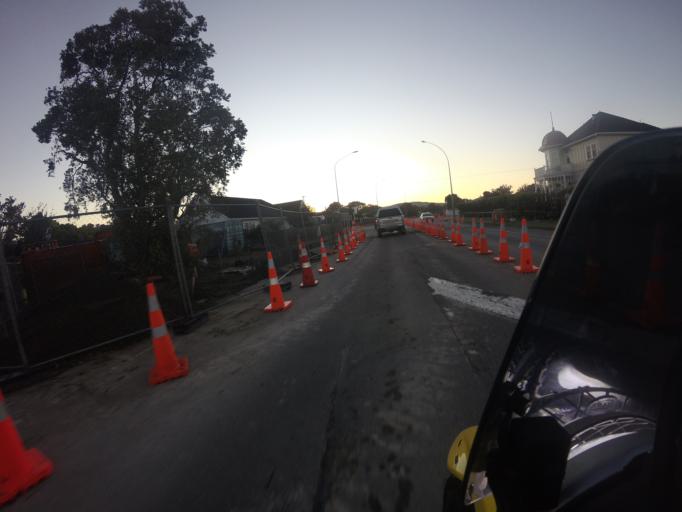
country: NZ
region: Gisborne
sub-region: Gisborne District
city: Gisborne
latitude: -38.6678
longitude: 178.0333
